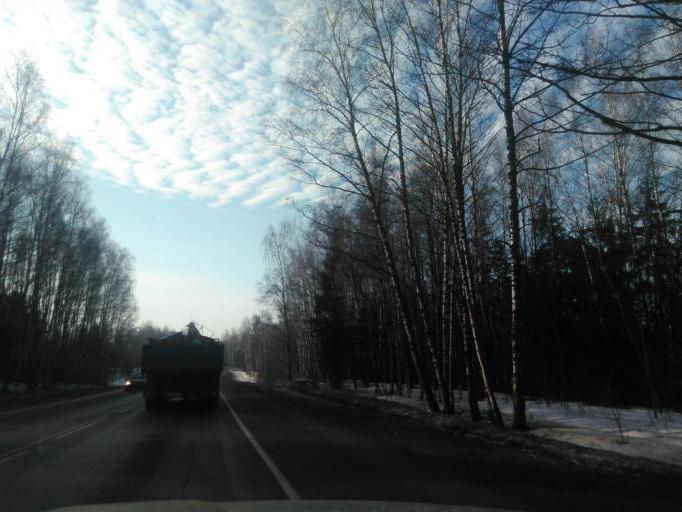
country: RU
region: Moskovskaya
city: Snegiri
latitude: 55.8902
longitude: 36.9443
